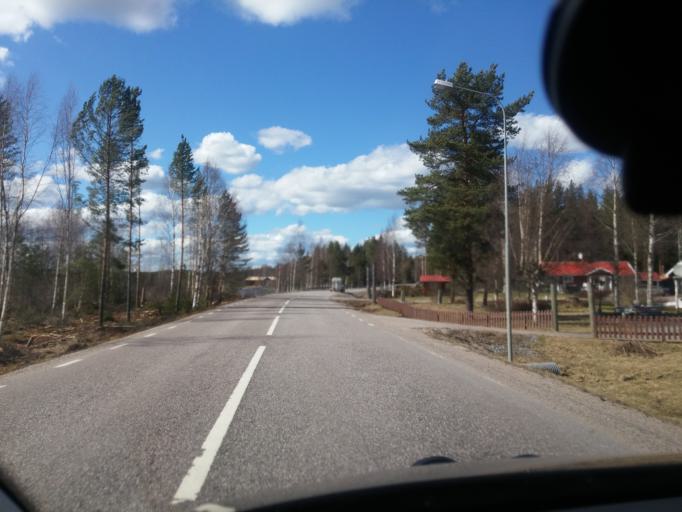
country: SE
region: Gaevleborg
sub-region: Ovanakers Kommun
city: Edsbyn
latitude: 61.2525
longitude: 15.8907
